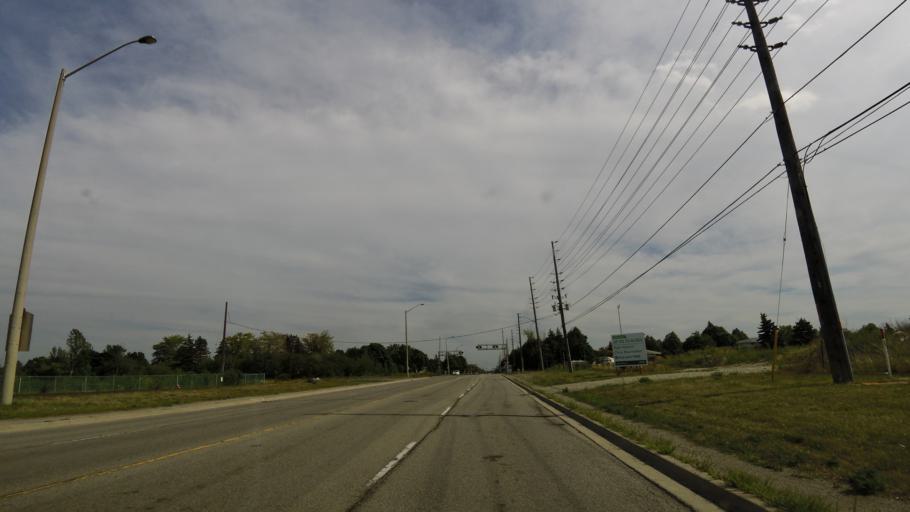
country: CA
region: Ontario
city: Etobicoke
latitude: 43.7282
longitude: -79.6516
